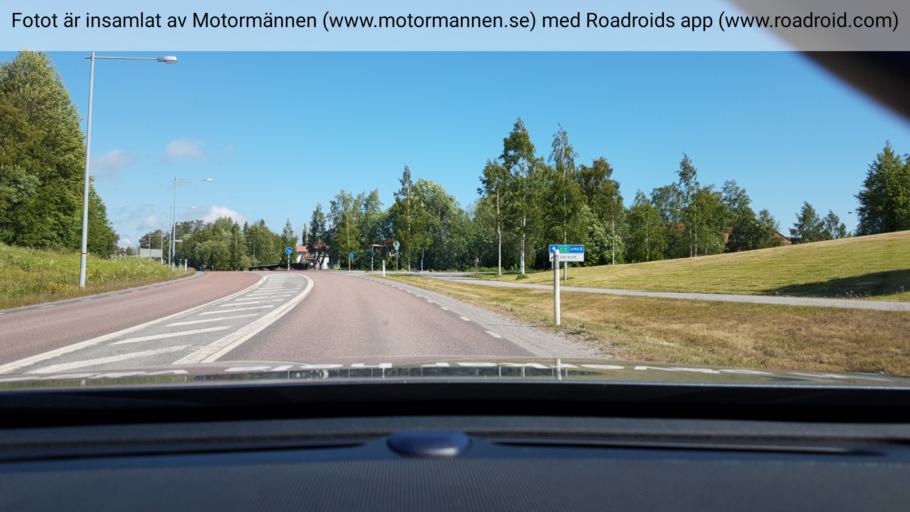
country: SE
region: Vaesterbotten
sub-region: Umea Kommun
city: Holmsund
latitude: 63.7049
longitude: 20.3614
